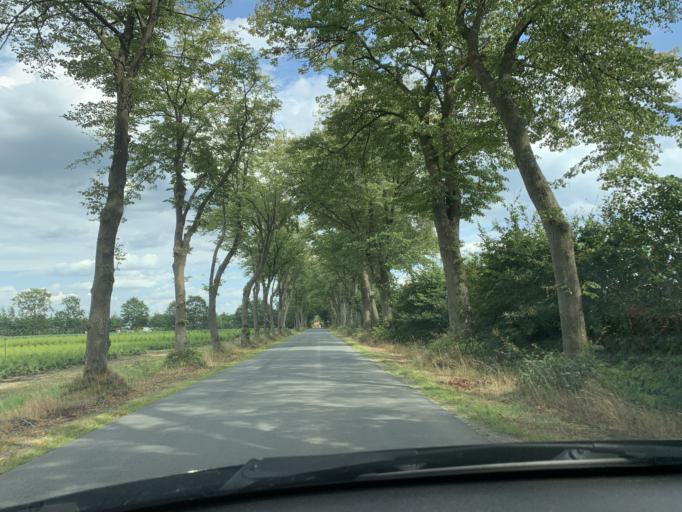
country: DE
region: Lower Saxony
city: Westerstede
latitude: 53.2565
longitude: 7.8698
